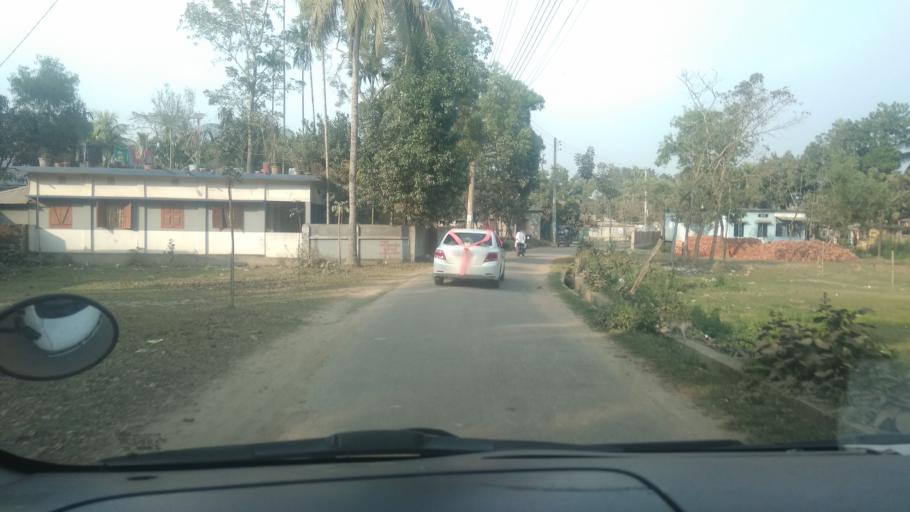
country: BD
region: Dhaka
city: Mymensingh
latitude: 24.7578
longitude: 90.5663
